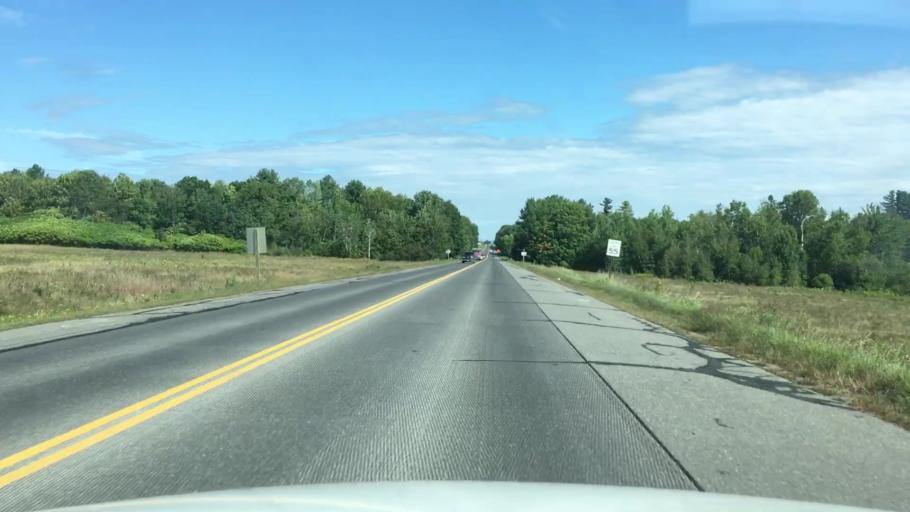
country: US
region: Maine
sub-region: Penobscot County
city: Newport
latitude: 44.8638
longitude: -69.2842
